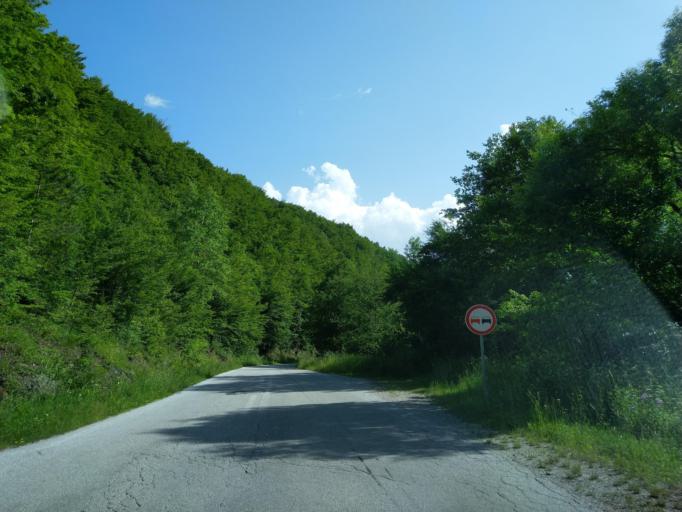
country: RS
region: Central Serbia
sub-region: Zlatiborski Okrug
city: Bajina Basta
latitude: 43.8622
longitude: 19.6256
